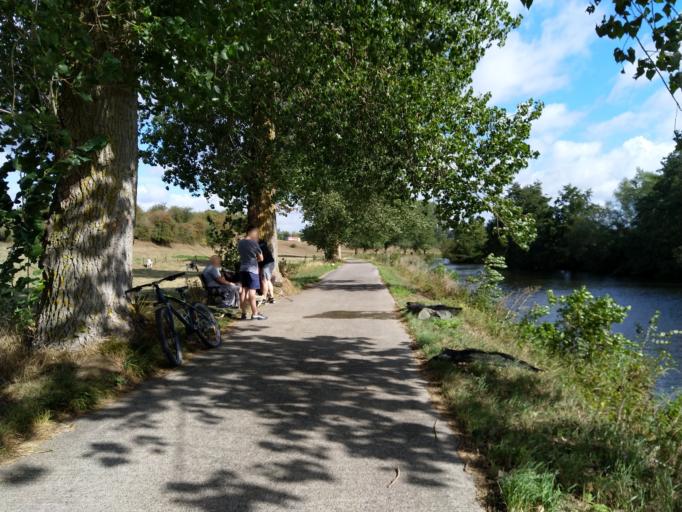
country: BE
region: Wallonia
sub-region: Province du Hainaut
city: Merbes-le-Chateau
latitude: 50.3149
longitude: 4.1499
